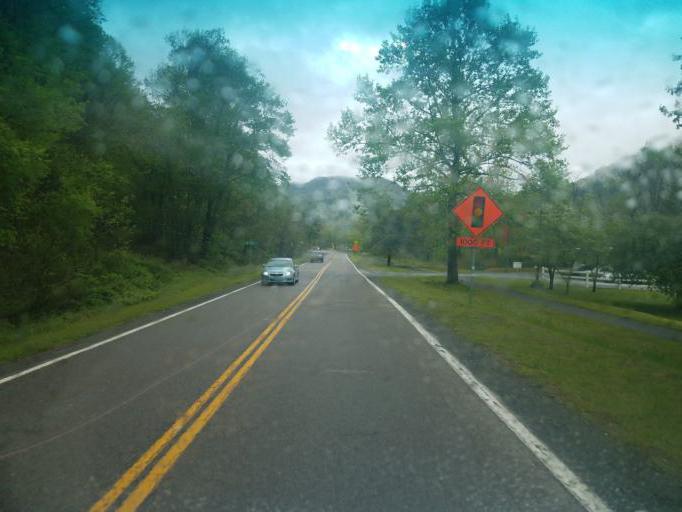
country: US
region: Tennessee
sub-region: Johnson County
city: Mountain City
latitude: 36.6270
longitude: -81.7749
